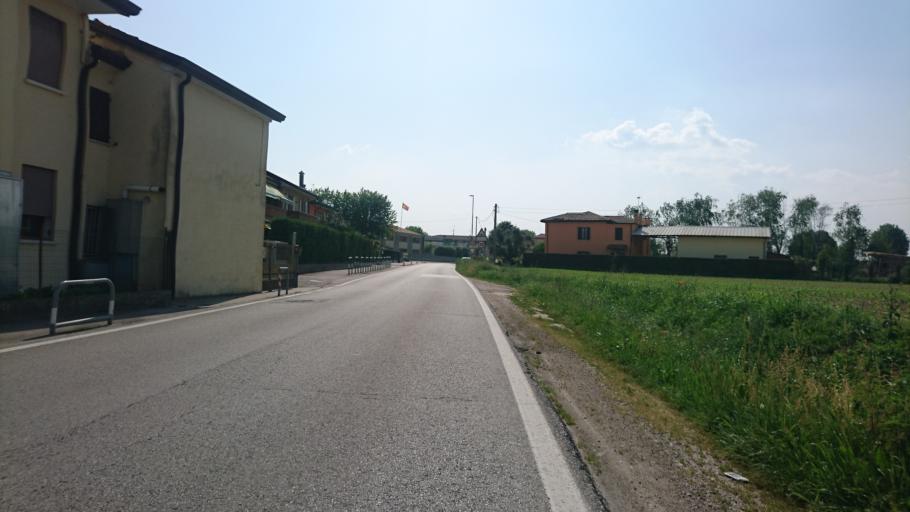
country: IT
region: Veneto
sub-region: Provincia di Padova
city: Villatora
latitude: 45.3865
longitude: 11.9748
